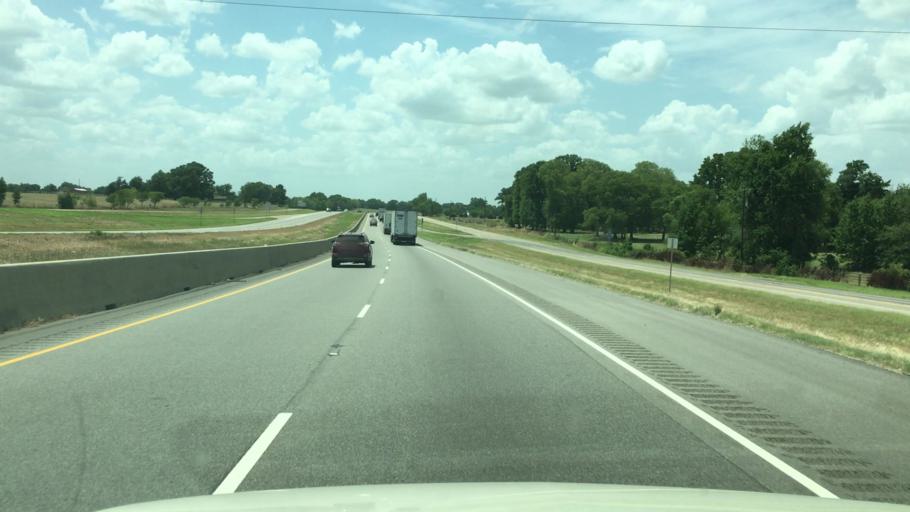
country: US
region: Texas
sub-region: Franklin County
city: Mount Vernon
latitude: 33.1623
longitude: -95.1783
